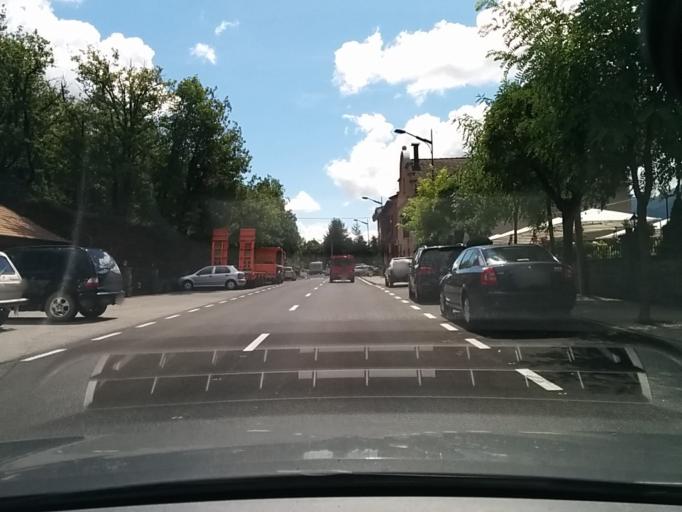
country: ES
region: Aragon
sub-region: Provincia de Huesca
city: Fiscal
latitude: 42.4987
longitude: -0.1157
